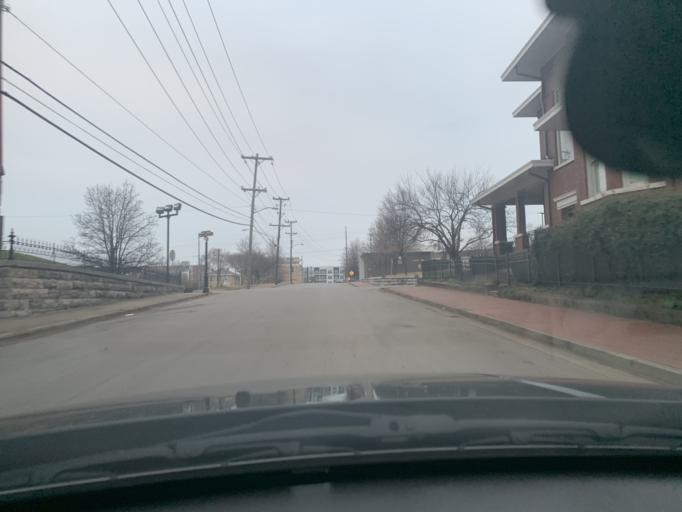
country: US
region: Tennessee
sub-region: Davidson County
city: Nashville
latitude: 36.1712
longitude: -86.7620
